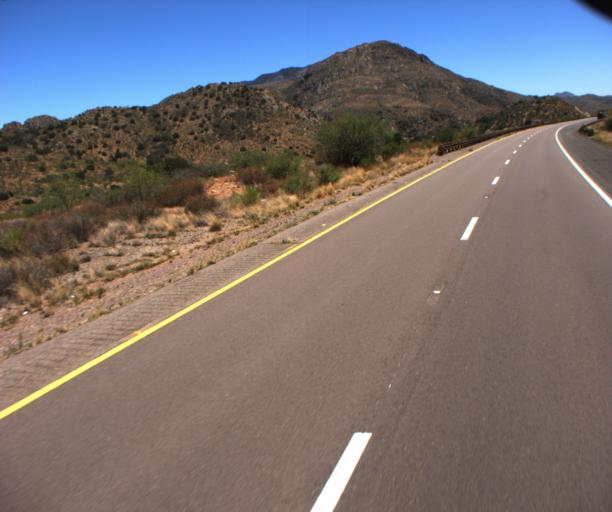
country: US
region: Arizona
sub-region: Gila County
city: Tonto Basin
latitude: 33.8542
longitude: -111.4720
